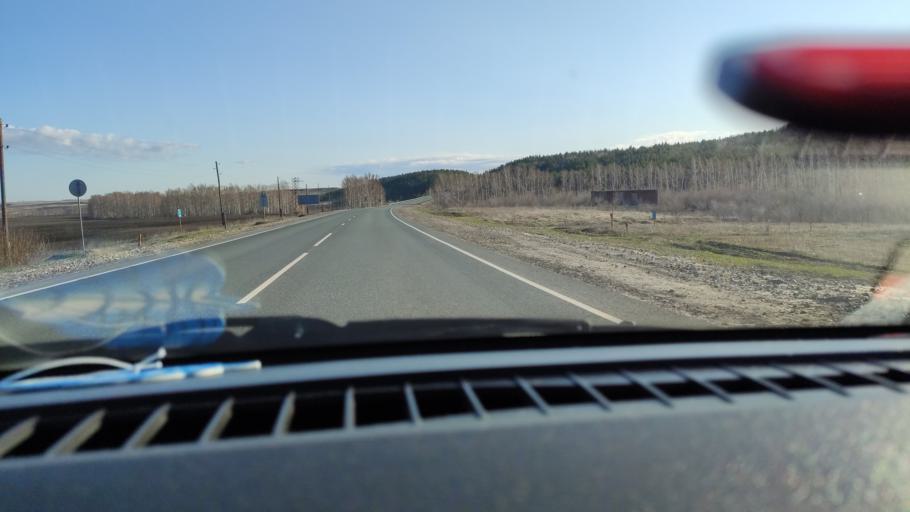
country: RU
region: Saratov
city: Khvalynsk
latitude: 52.5267
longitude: 48.0245
